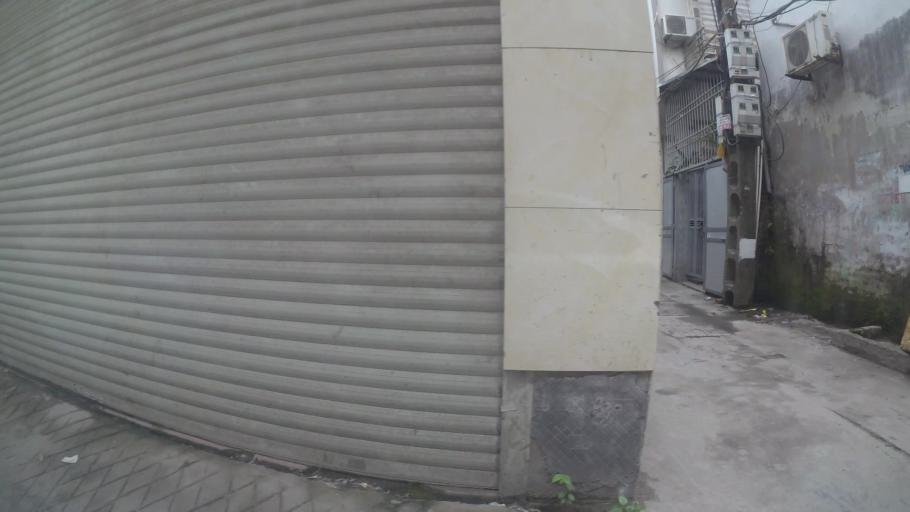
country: VN
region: Ha Noi
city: Tay Ho
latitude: 21.0739
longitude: 105.7888
